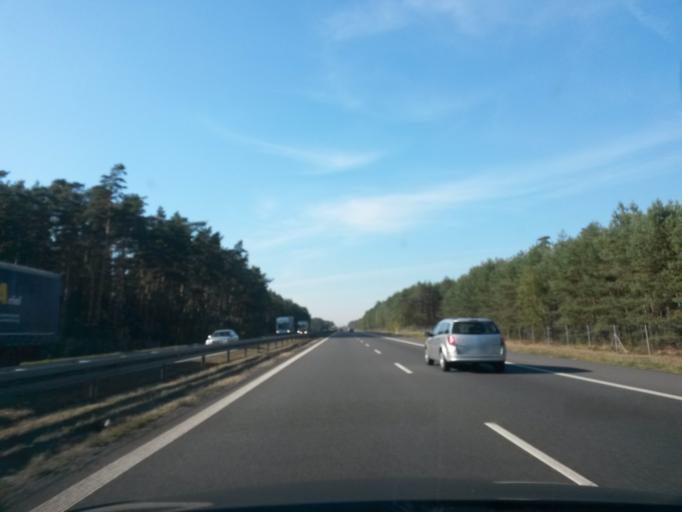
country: PL
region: Opole Voivodeship
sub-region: Powiat opolski
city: Komprachcice
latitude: 50.6094
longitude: 17.7793
